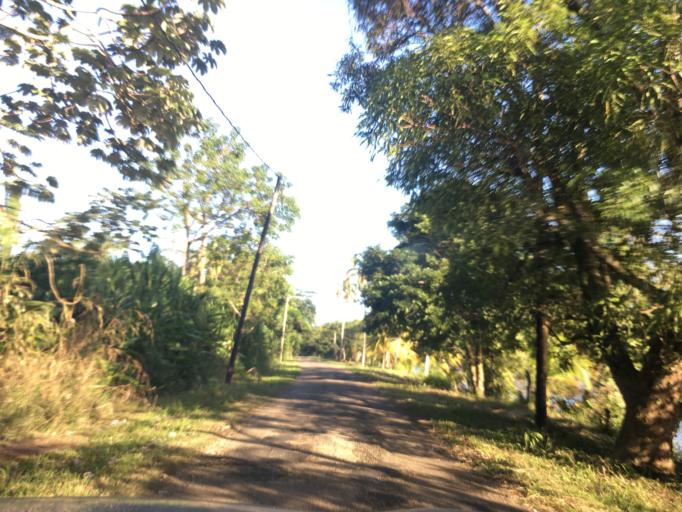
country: BZ
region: Stann Creek
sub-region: Dangriga
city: Dangriga
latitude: 16.8244
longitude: -88.3069
